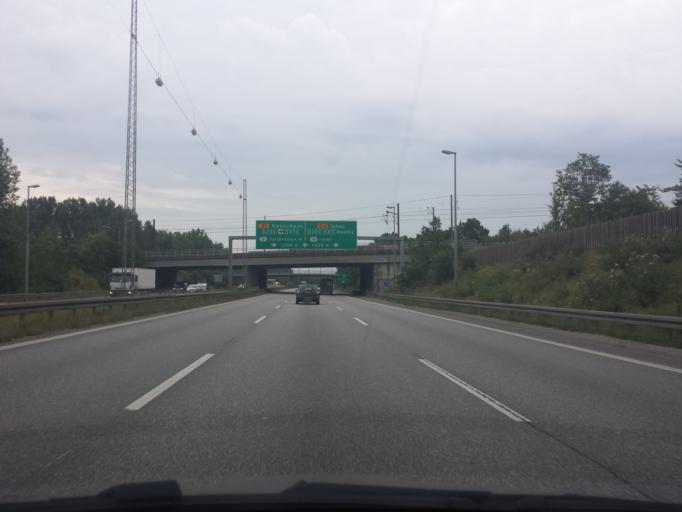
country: DK
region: Capital Region
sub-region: Hoje-Taastrup Kommune
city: Taastrup
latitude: 55.6553
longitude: 12.3216
